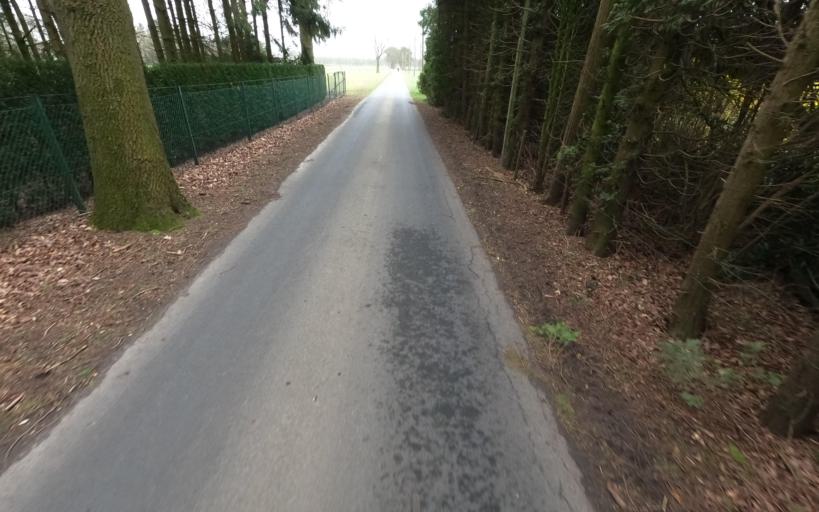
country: BE
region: Flanders
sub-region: Provincie Antwerpen
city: Essen
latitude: 51.4220
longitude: 4.4119
